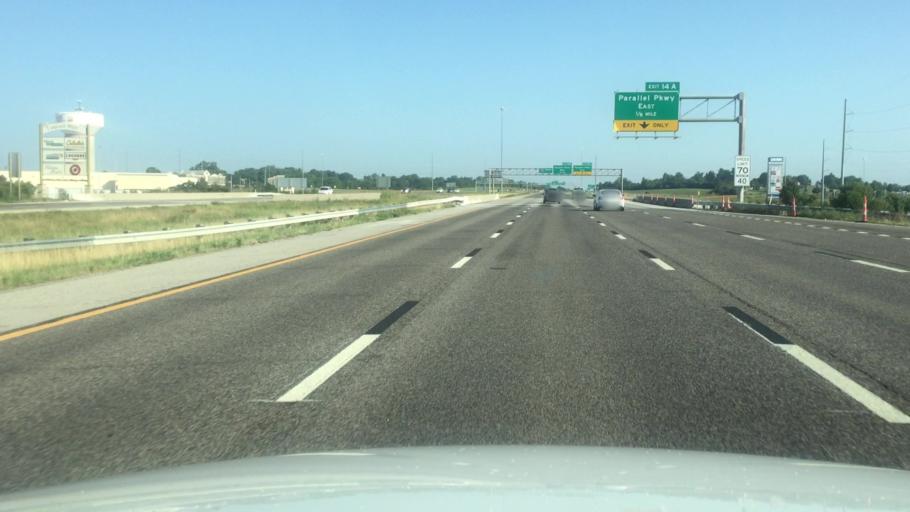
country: US
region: Kansas
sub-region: Wyandotte County
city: Edwardsville
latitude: 39.1222
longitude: -94.8133
